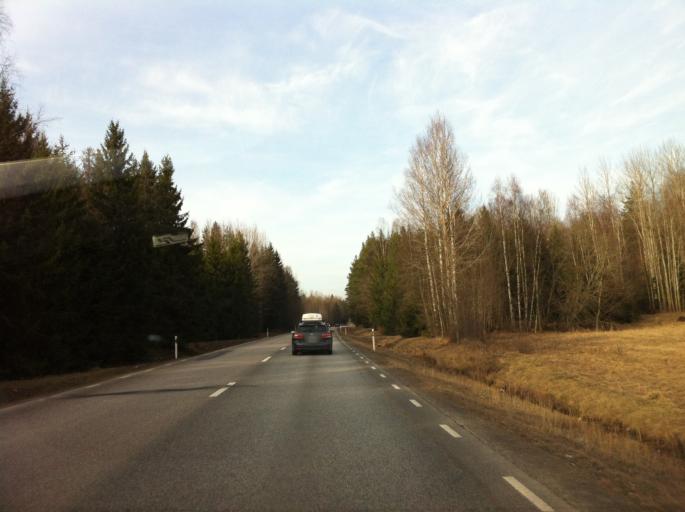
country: SE
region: Vaermland
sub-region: Kristinehamns Kommun
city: Bjorneborg
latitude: 59.1416
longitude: 14.1760
